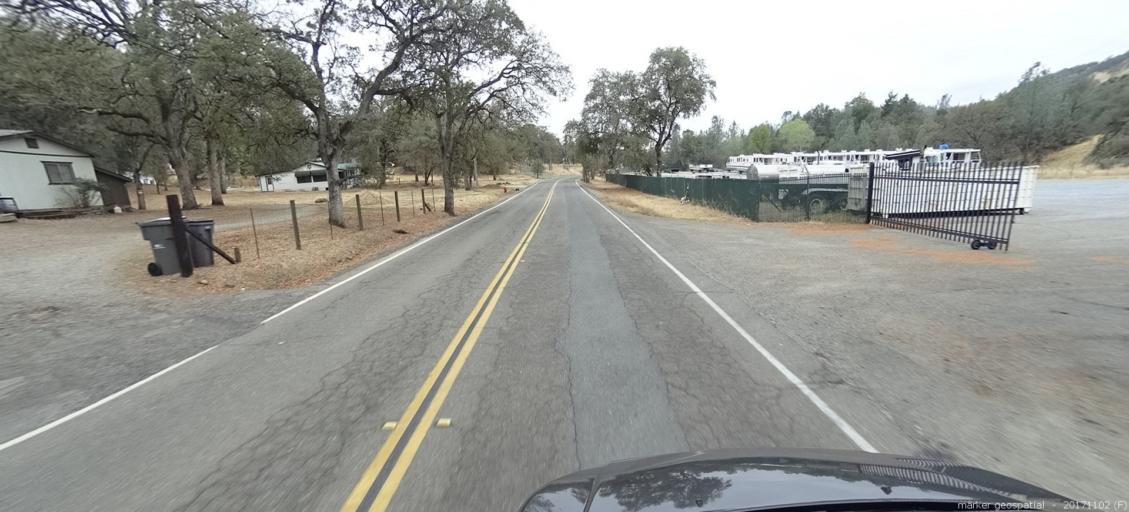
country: US
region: California
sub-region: Shasta County
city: Bella Vista
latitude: 40.7115
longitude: -122.2424
